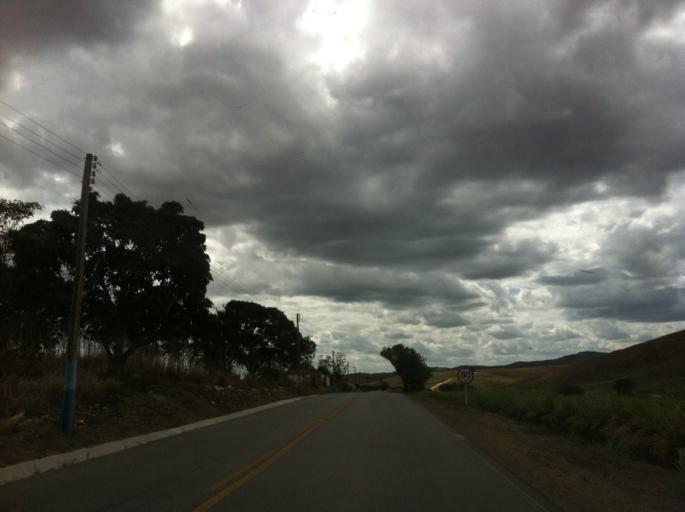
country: BR
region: Alagoas
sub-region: Ibateguara
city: Ibateguara
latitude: -8.9623
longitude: -35.9400
